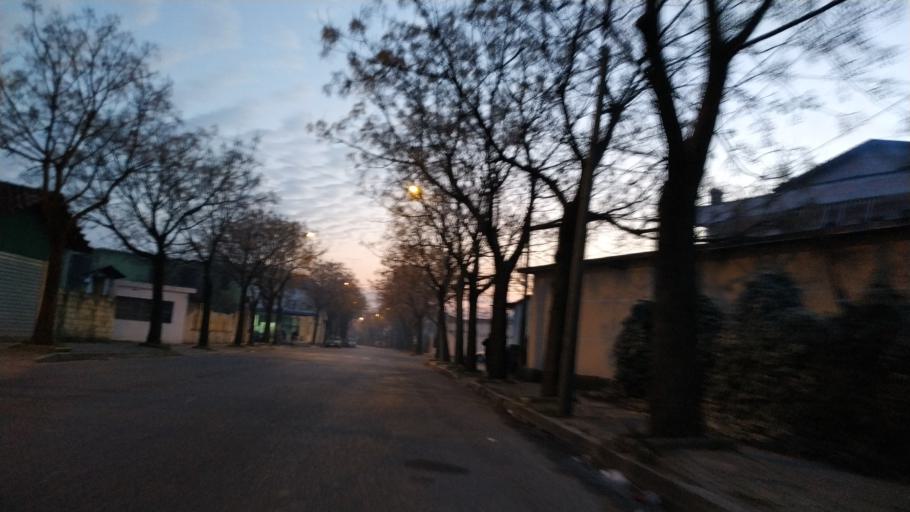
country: AL
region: Shkoder
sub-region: Rrethi i Shkodres
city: Shkoder
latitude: 42.0764
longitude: 19.5034
